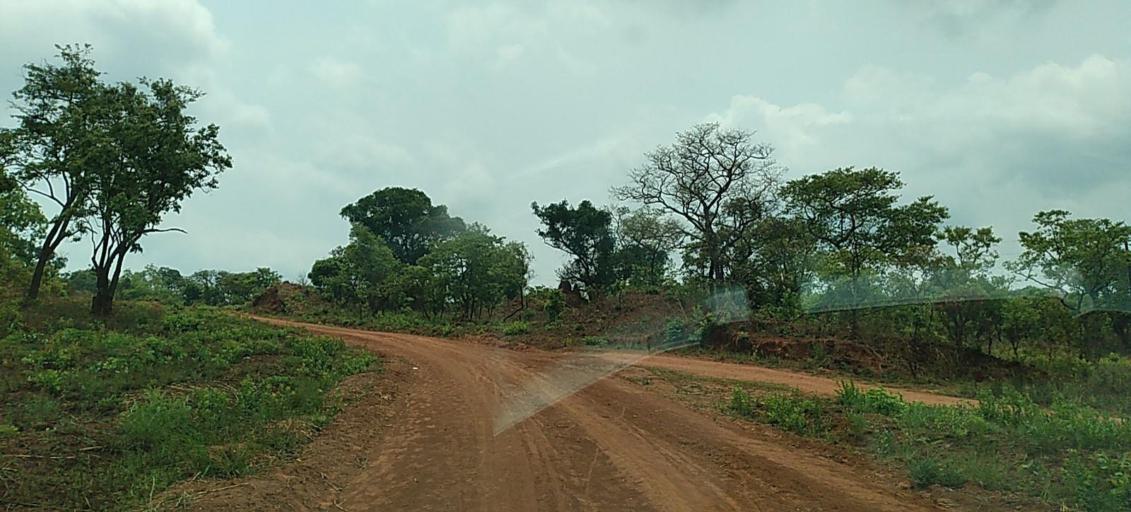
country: ZM
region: North-Western
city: Mwinilunga
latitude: -11.4568
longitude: 24.7598
